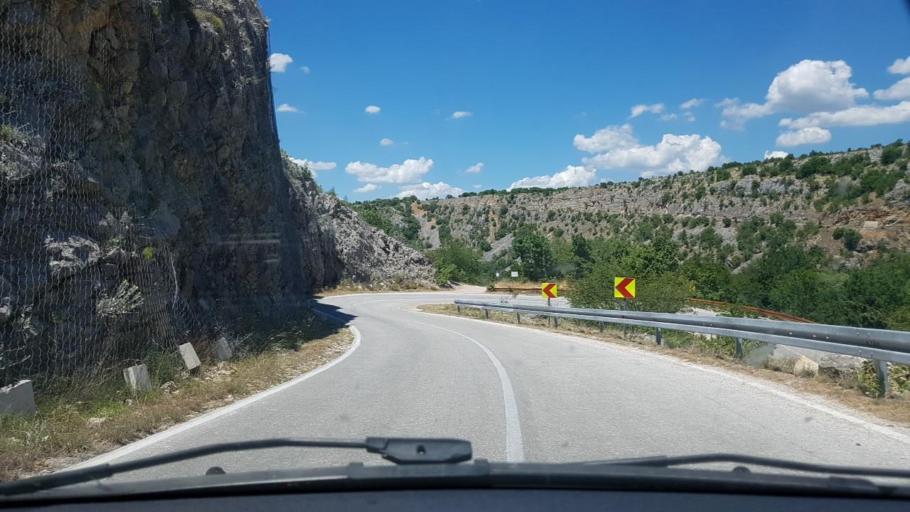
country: HR
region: Sibensko-Kniniska
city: Kistanje
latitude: 44.0102
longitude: 16.0349
